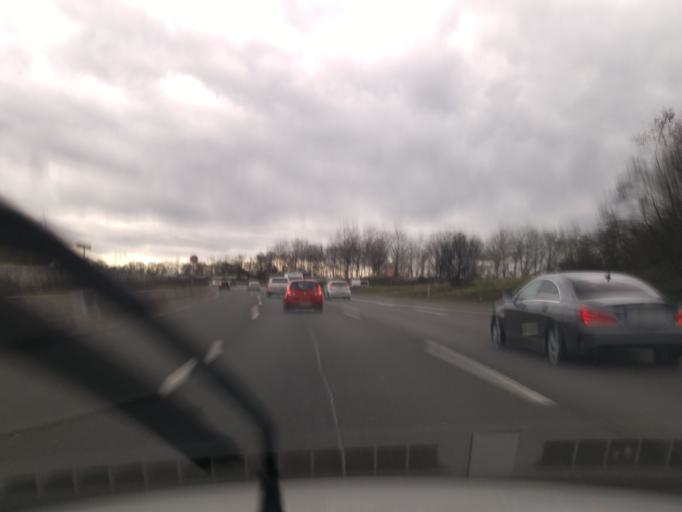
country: DE
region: North Rhine-Westphalia
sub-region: Regierungsbezirk Dusseldorf
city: Dusseldorf
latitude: 51.1910
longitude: 6.7791
